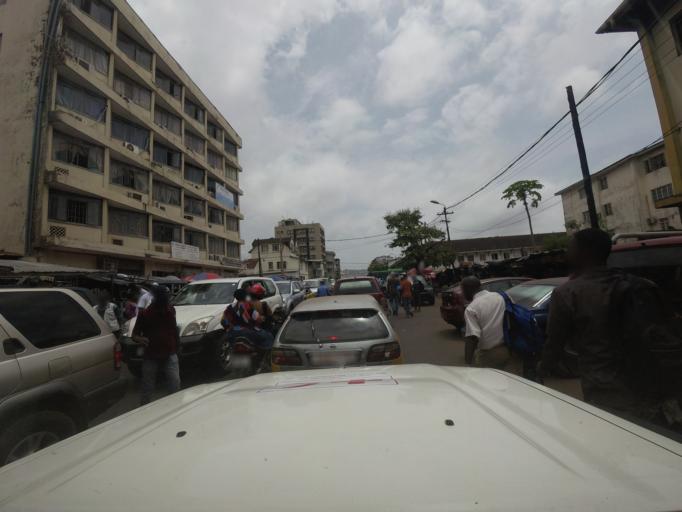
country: SL
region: Western Area
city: Freetown
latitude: 8.4881
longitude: -13.2374
